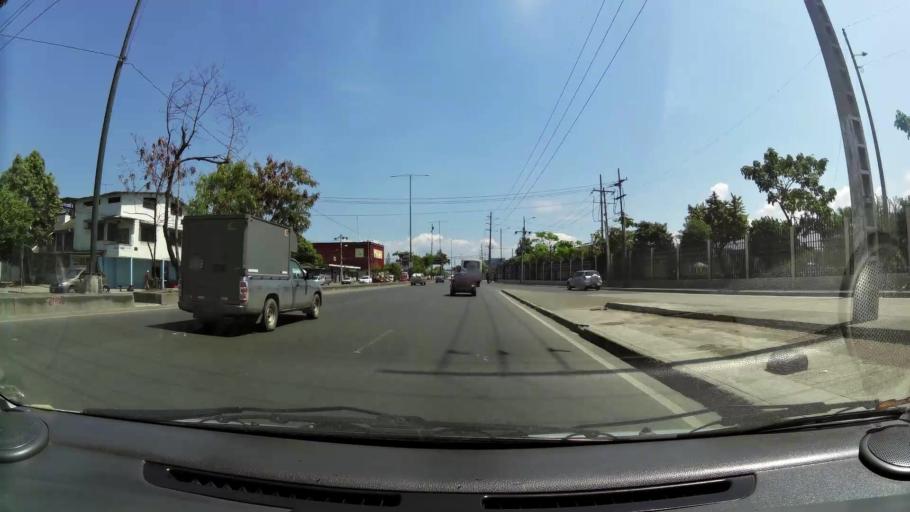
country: EC
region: Guayas
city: Guayaquil
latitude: -2.2388
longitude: -79.9003
